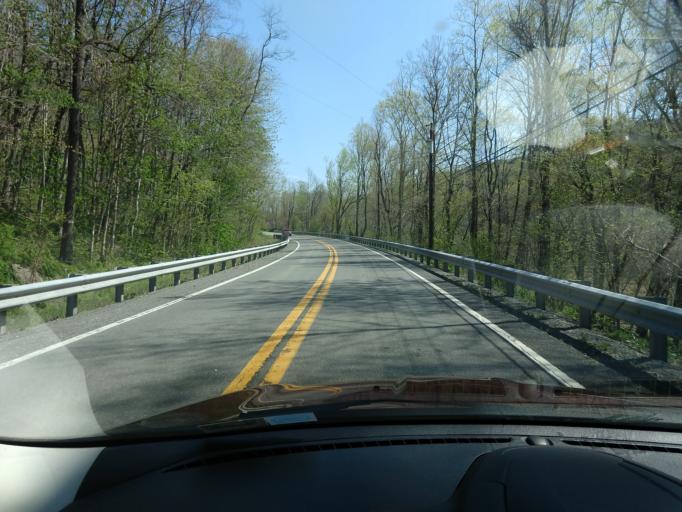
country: US
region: West Virginia
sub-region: Greenbrier County
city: Alderson
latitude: 37.7173
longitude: -80.6161
